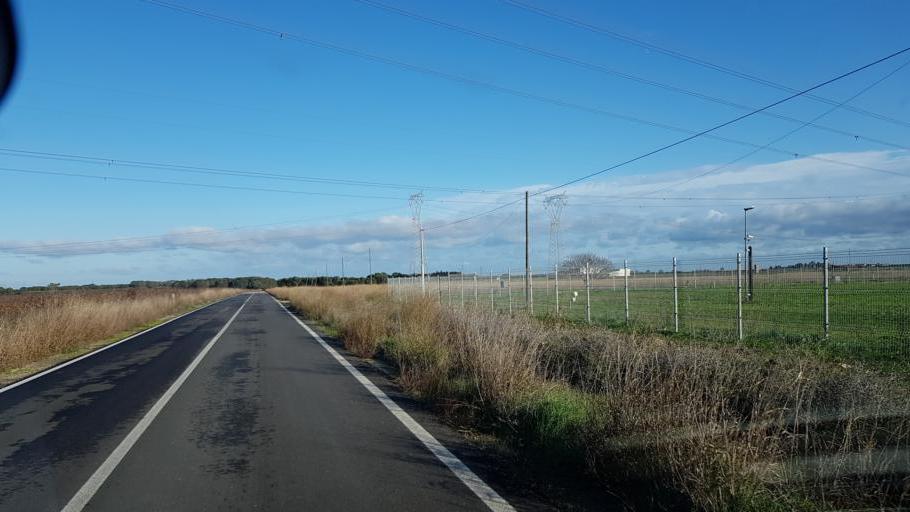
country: IT
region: Apulia
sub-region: Provincia di Brindisi
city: Tuturano
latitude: 40.5567
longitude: 17.9475
